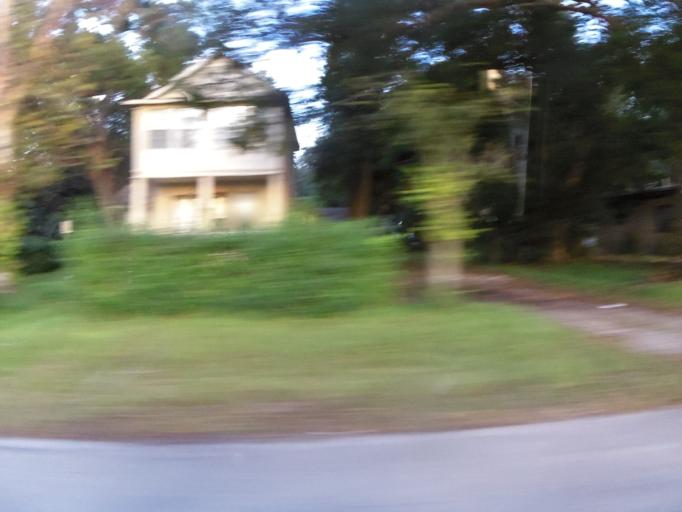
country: US
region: Florida
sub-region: Duval County
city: Jacksonville
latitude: 30.3530
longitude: -81.7229
